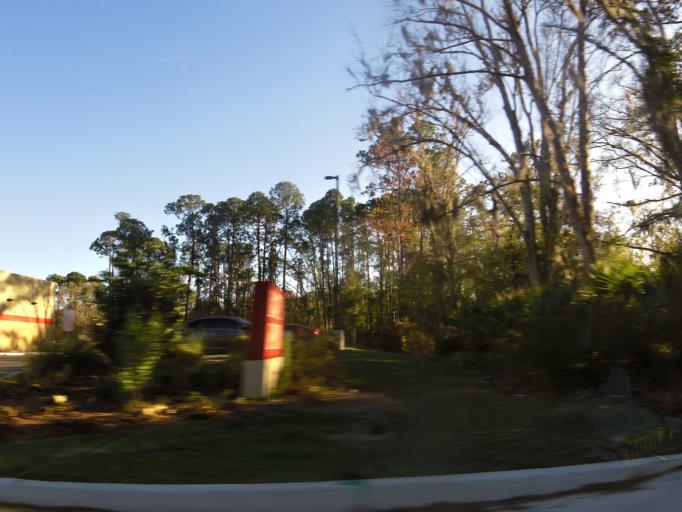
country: US
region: Florida
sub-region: Saint Johns County
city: Fruit Cove
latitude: 30.2059
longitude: -81.5961
